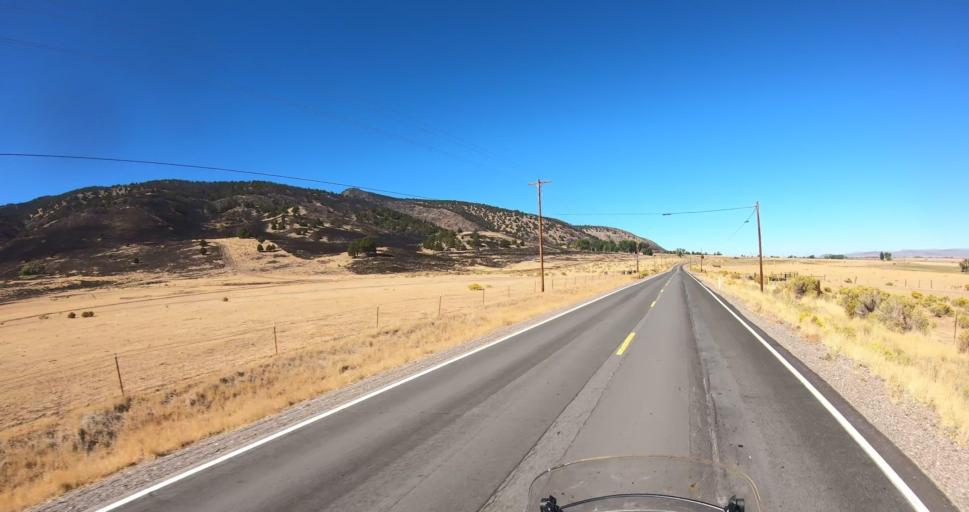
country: US
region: Oregon
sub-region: Lake County
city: Lakeview
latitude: 42.6347
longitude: -120.5169
